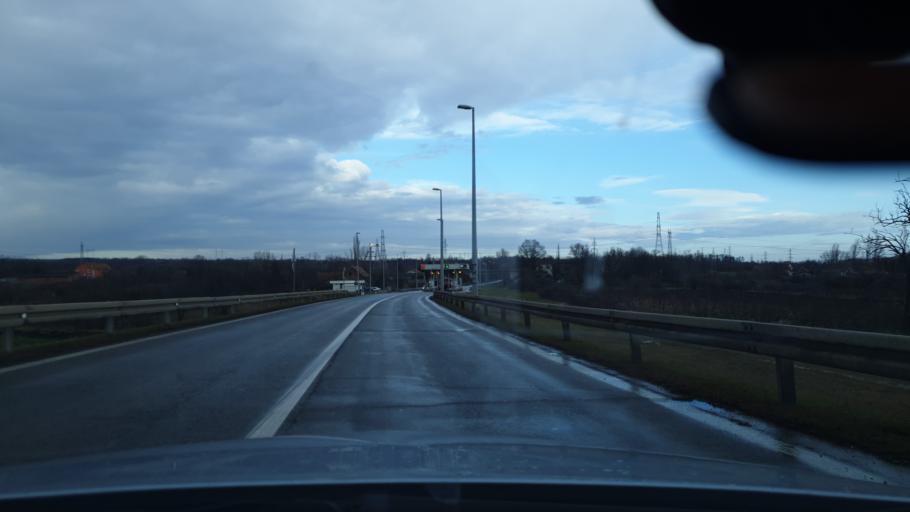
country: RS
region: Central Serbia
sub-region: Podunavski Okrug
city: Smederevo
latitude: 44.5885
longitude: 20.9578
